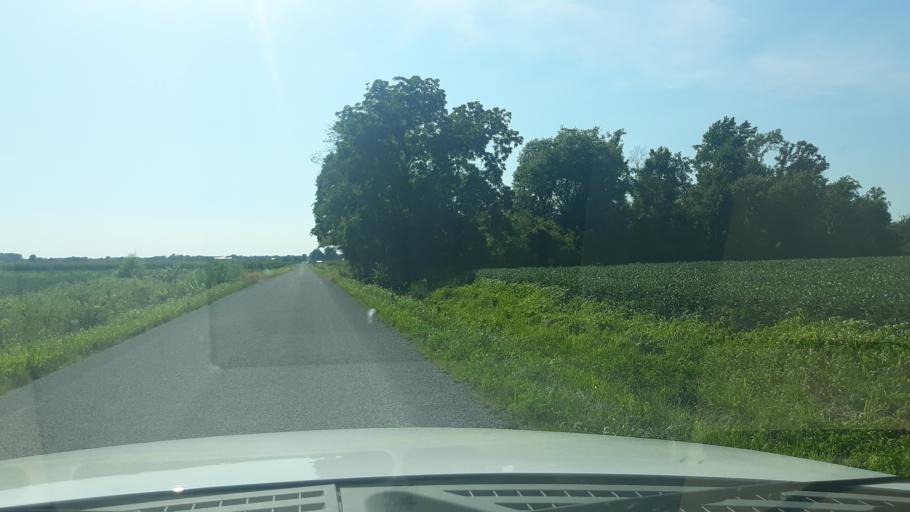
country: US
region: Illinois
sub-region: Saline County
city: Eldorado
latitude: 37.8631
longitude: -88.4914
